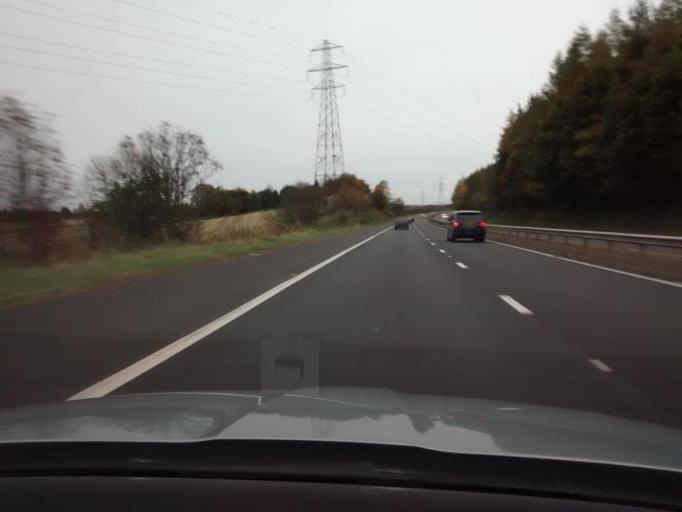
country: GB
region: Scotland
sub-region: Stirling
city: Cowie
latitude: 56.0657
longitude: -3.8694
